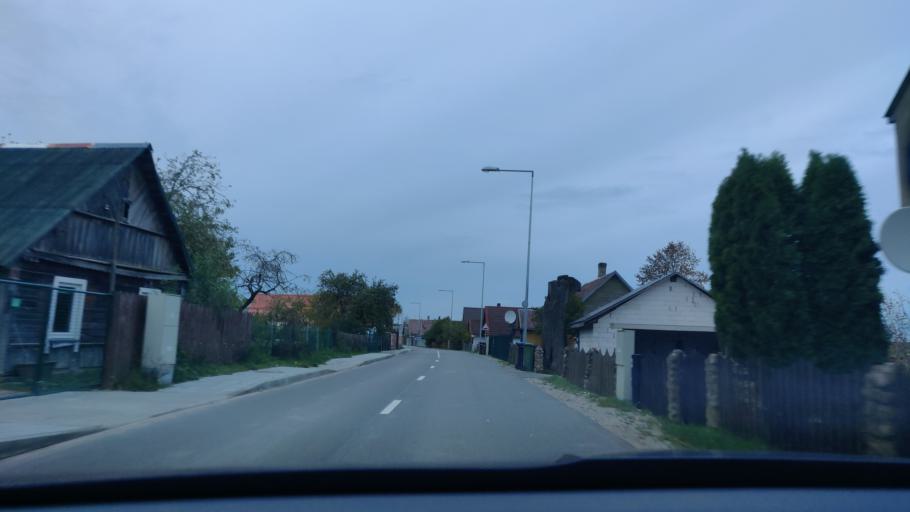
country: LT
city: Lentvaris
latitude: 54.5857
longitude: 25.0513
